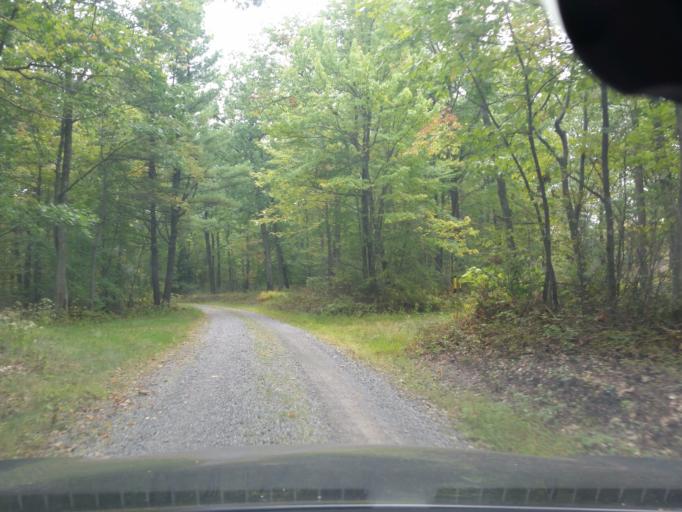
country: US
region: Pennsylvania
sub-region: Lycoming County
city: Jersey Shore
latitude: 41.0910
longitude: -77.1948
